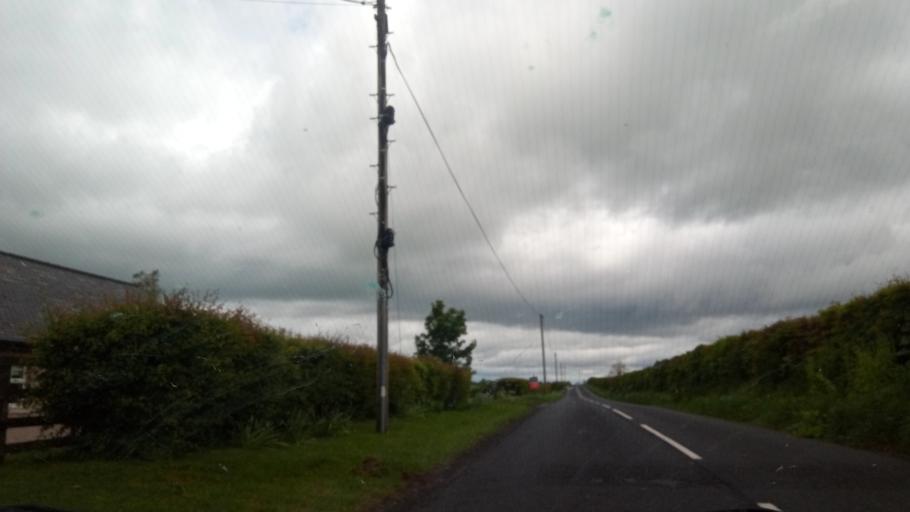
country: GB
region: Scotland
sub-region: The Scottish Borders
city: Hawick
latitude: 55.4490
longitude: -2.7627
